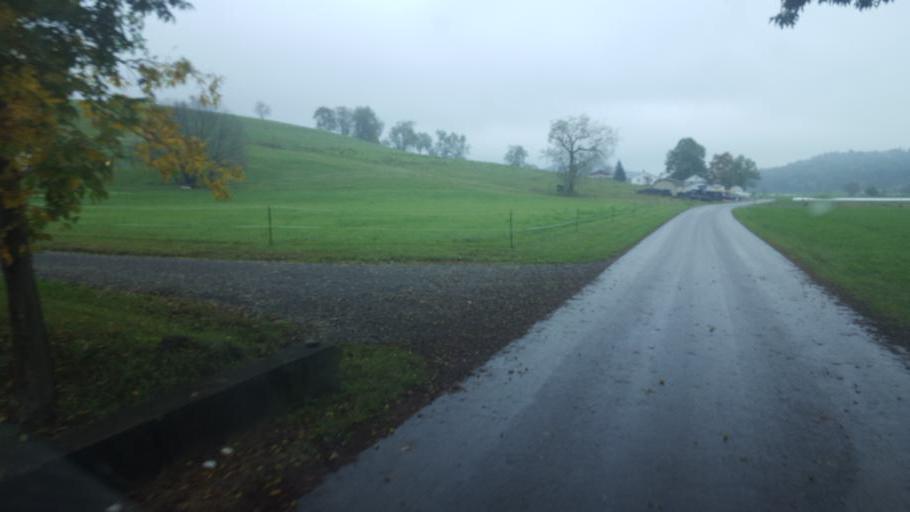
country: US
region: Ohio
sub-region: Tuscarawas County
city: Sugarcreek
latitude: 40.5876
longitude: -81.7437
